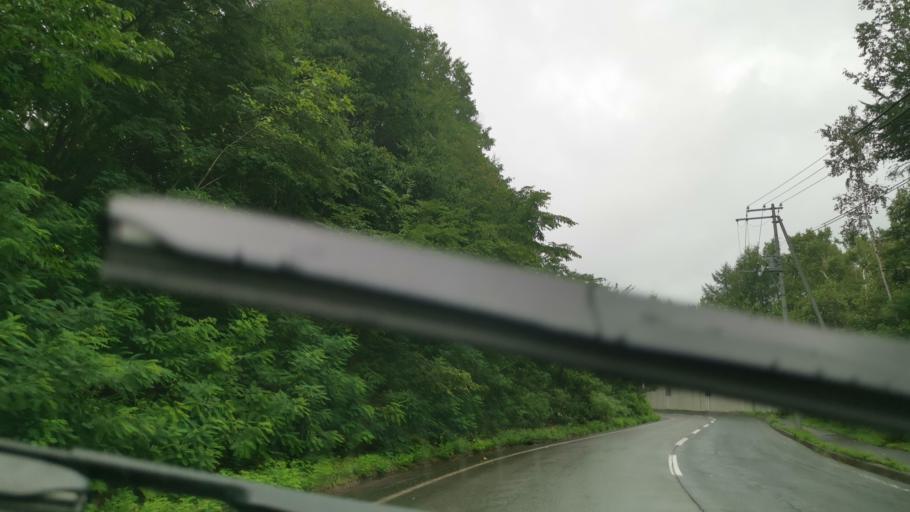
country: JP
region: Hokkaido
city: Sapporo
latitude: 42.9479
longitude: 141.3575
